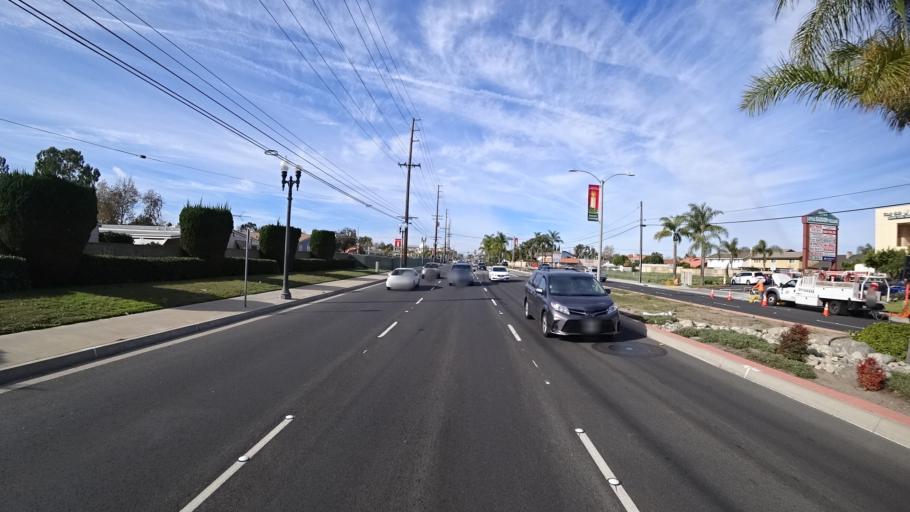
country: US
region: California
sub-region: Orange County
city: Garden Grove
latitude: 33.7449
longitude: -117.9521
